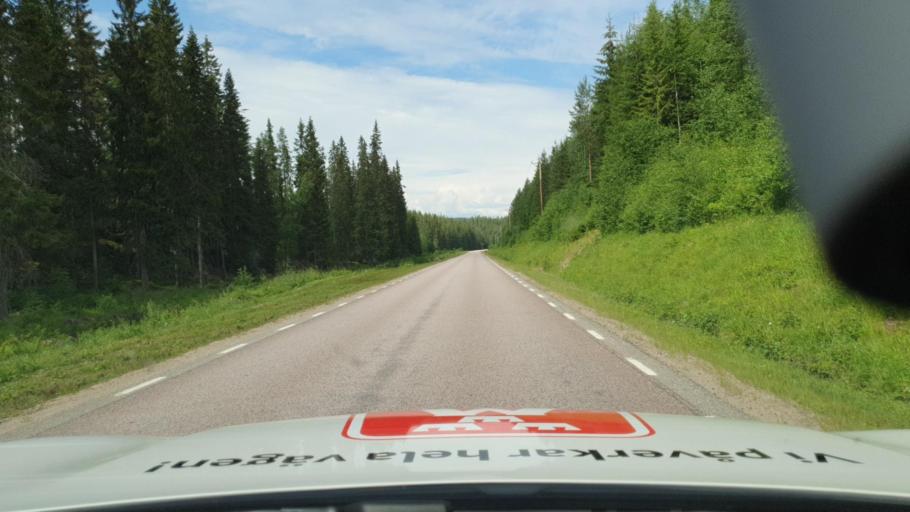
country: SE
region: Vaermland
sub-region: Torsby Kommun
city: Torsby
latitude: 60.7431
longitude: 12.7009
